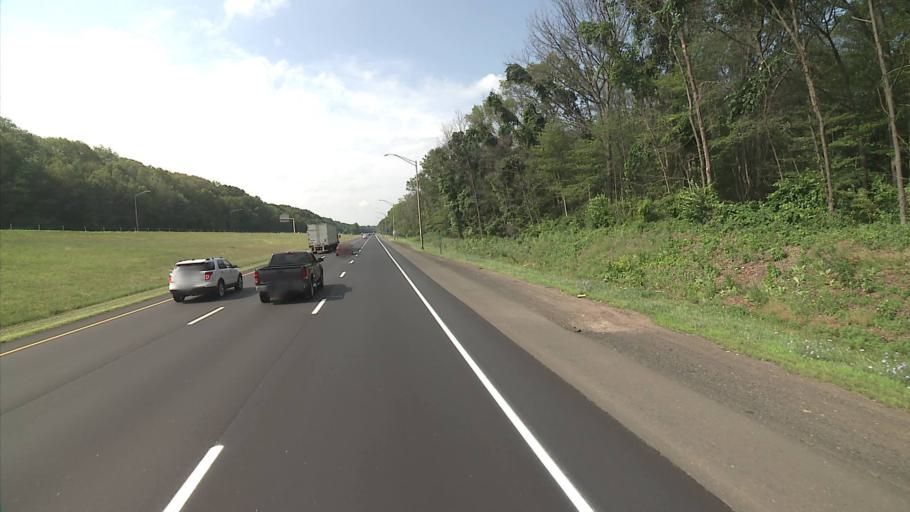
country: US
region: Connecticut
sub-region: New Haven County
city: Wallingford Center
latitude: 41.4169
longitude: -72.8294
